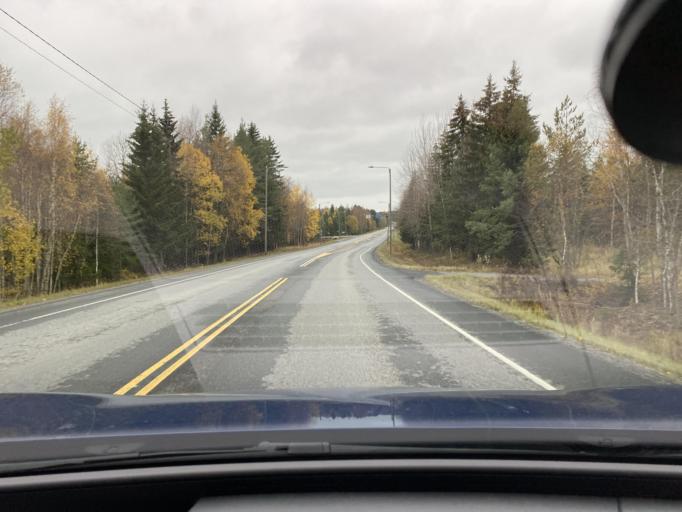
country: FI
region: Satakunta
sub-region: Rauma
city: Rauma
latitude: 61.1278
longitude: 21.6065
